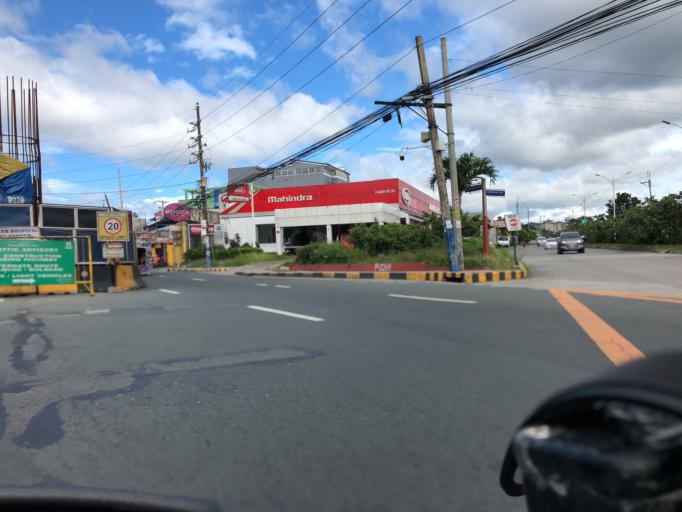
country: PH
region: Calabarzon
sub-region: Province of Rizal
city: San Mateo
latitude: 14.7295
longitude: 121.0612
